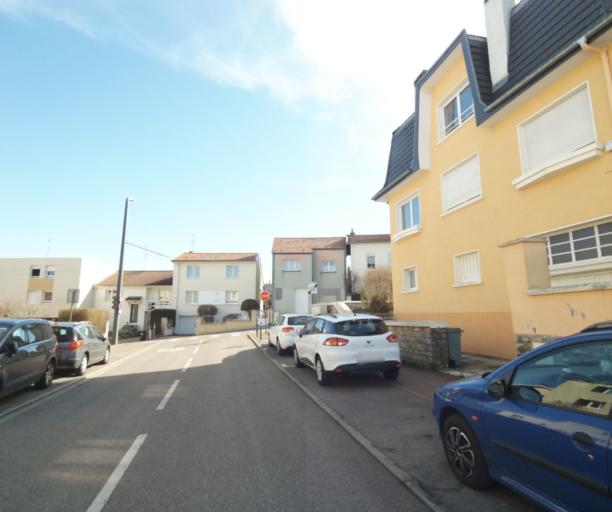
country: FR
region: Lorraine
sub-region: Departement de Meurthe-et-Moselle
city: Villers-les-Nancy
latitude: 48.6636
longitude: 6.1626
